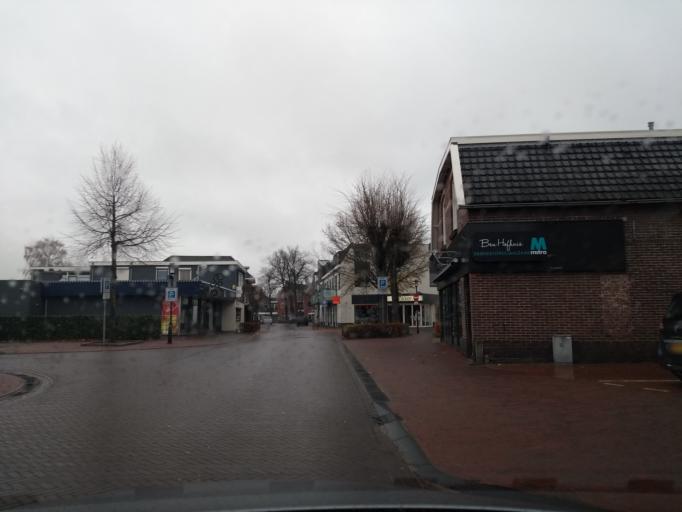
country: NL
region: Overijssel
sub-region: Gemeente Wierden
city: Wierden
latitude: 52.3589
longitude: 6.5894
